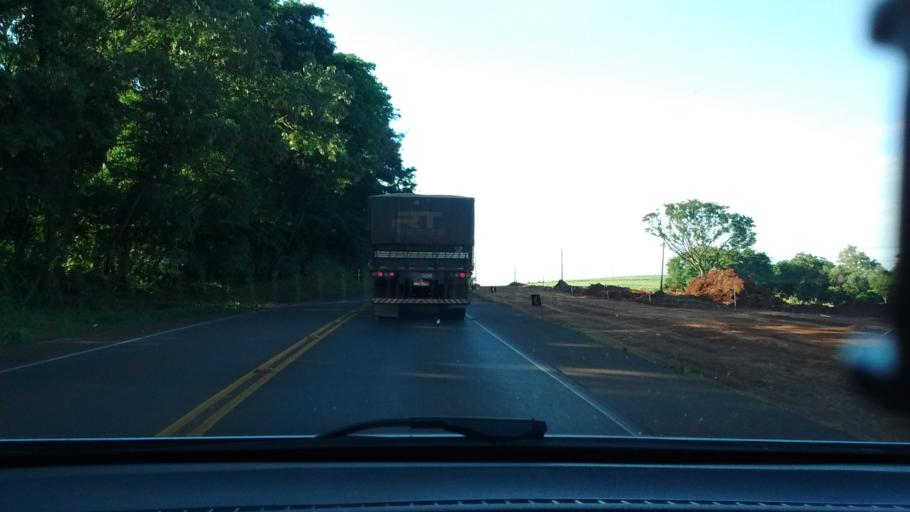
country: BR
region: Parana
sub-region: Cascavel
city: Cascavel
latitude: -25.2151
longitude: -53.5957
